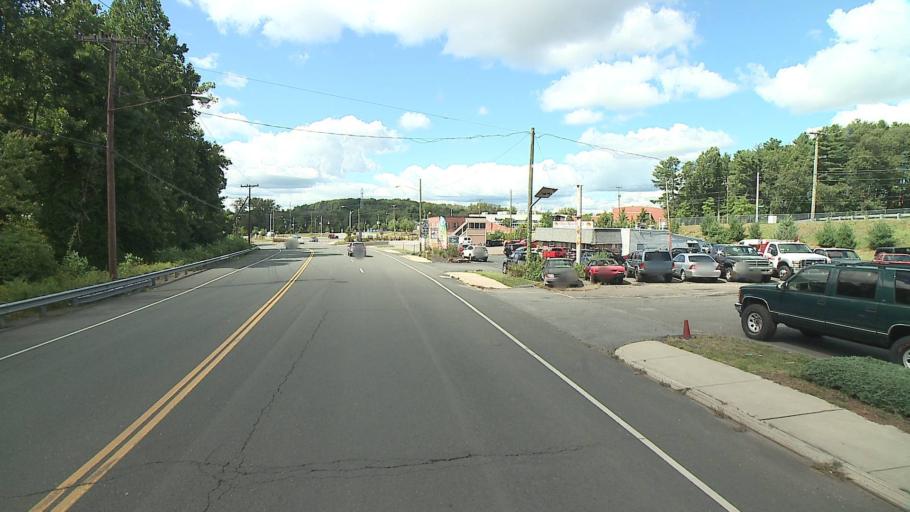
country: US
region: Connecticut
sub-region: Hartford County
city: Manchester
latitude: 41.7803
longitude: -72.5593
